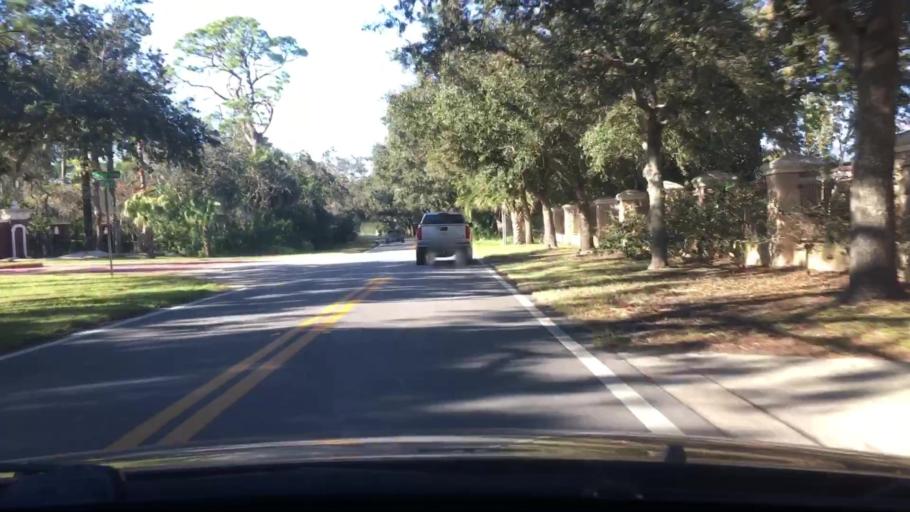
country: US
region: Florida
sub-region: Volusia County
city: Ormond-by-the-Sea
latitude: 29.3490
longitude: -81.0967
